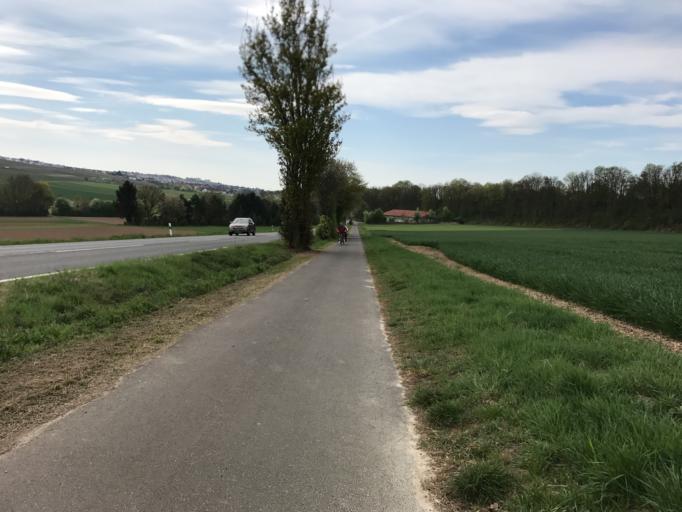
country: DE
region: Rheinland-Pfalz
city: Nieder-Olm
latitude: 49.9236
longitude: 8.2054
